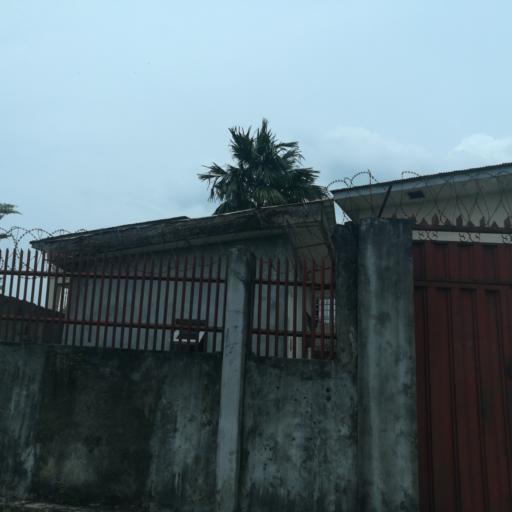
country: NG
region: Rivers
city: Port Harcourt
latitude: 4.7958
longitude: 7.0052
